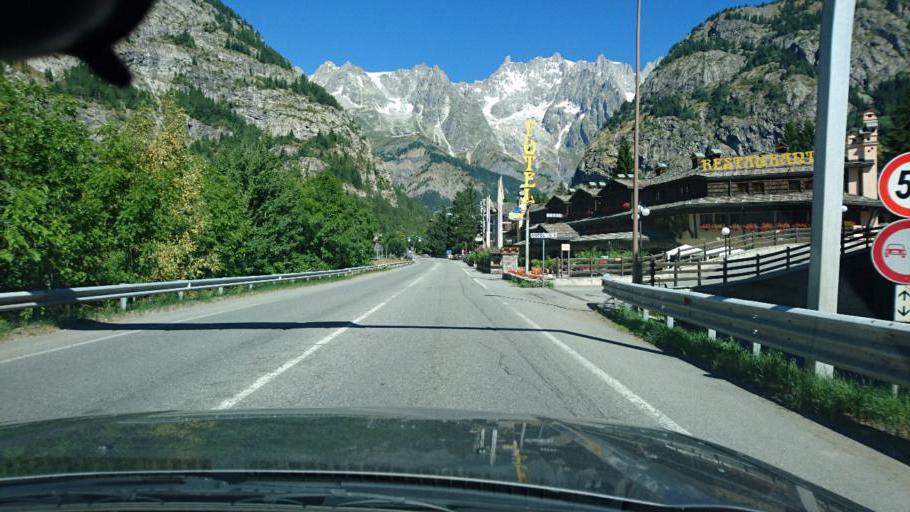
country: IT
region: Aosta Valley
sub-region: Valle d'Aosta
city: Courmayeur
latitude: 45.7917
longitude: 6.9694
